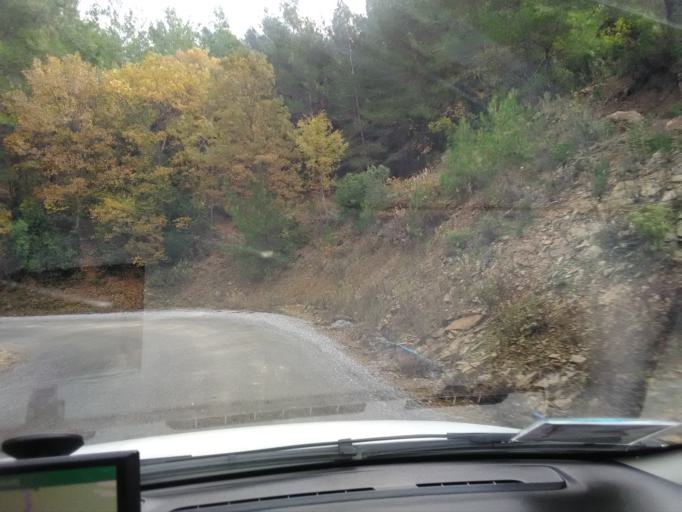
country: TR
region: Antalya
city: Gazipasa
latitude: 36.2463
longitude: 32.4378
